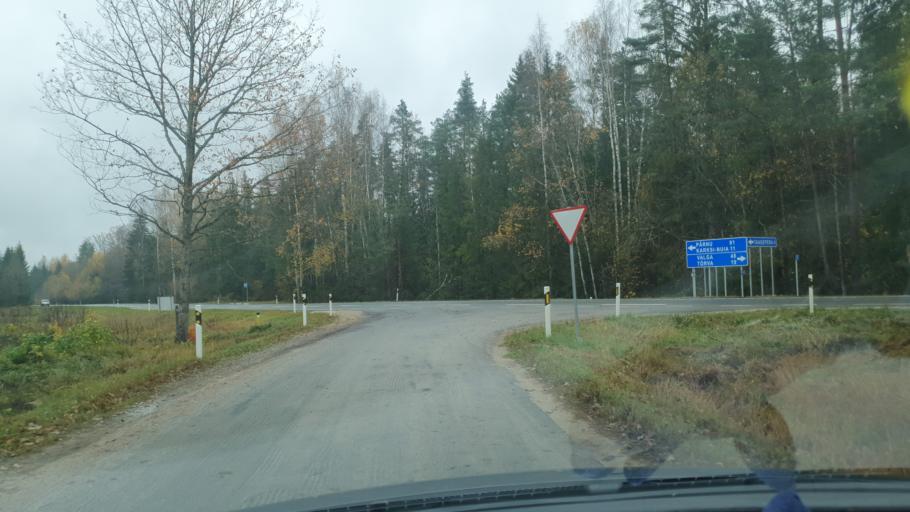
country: EE
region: Viljandimaa
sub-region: Karksi vald
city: Karksi-Nuia
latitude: 58.0293
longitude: 25.6521
